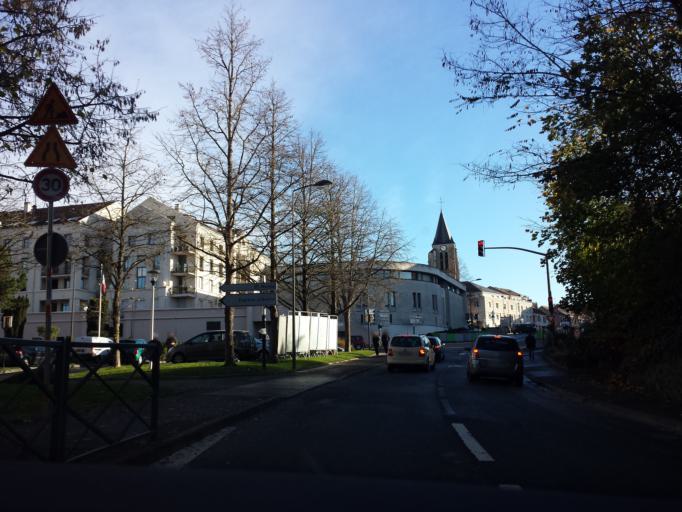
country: FR
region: Ile-de-France
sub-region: Departement de l'Essonne
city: Massy
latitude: 48.7304
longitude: 2.2713
